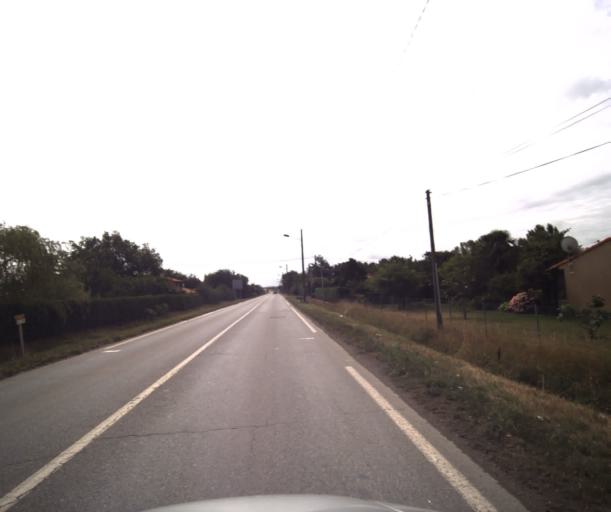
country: FR
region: Midi-Pyrenees
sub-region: Departement de la Haute-Garonne
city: Pinsaguel
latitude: 43.5279
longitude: 1.3747
